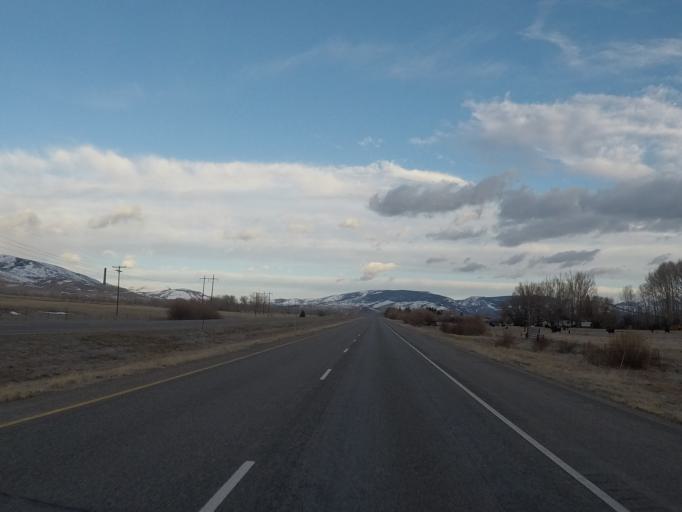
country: US
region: Montana
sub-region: Deer Lodge County
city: Warm Springs
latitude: 46.1022
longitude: -112.8382
